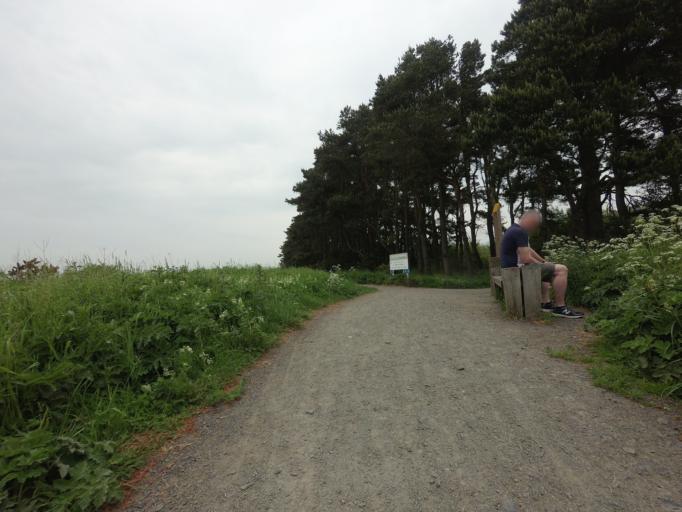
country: GB
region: Scotland
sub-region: Perth and Kinross
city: Milnathort
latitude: 56.2154
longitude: -3.3607
